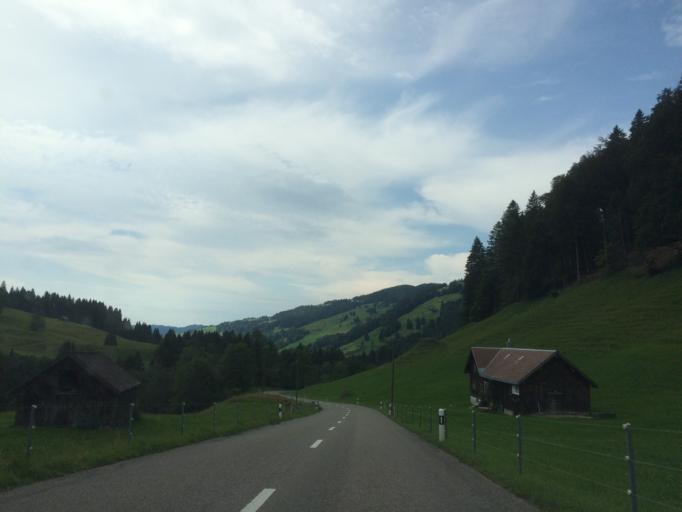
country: CH
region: Appenzell Ausserrhoden
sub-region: Bezirk Hinterland
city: Urnasch
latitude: 47.2429
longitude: 9.2669
